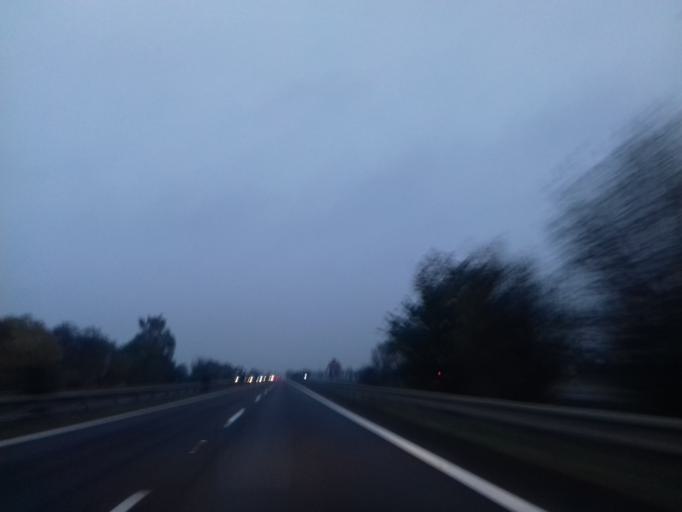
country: CZ
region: Olomoucky
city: Naklo
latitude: 49.6541
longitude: 17.1180
